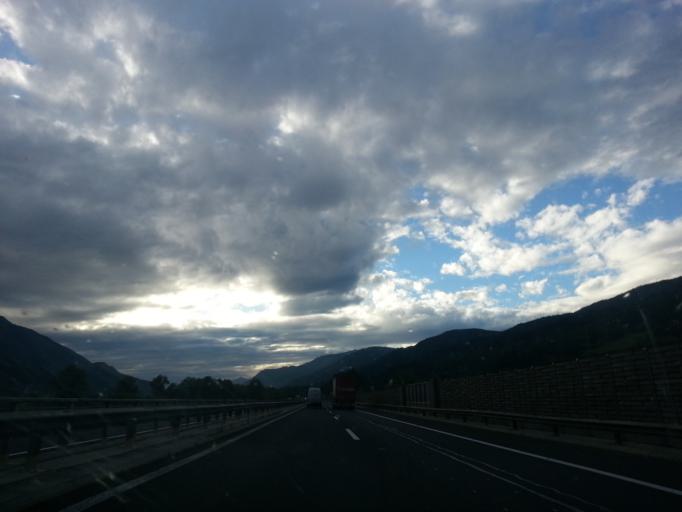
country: AT
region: Styria
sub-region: Politischer Bezirk Liezen
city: Trieben
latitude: 47.4933
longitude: 14.5008
